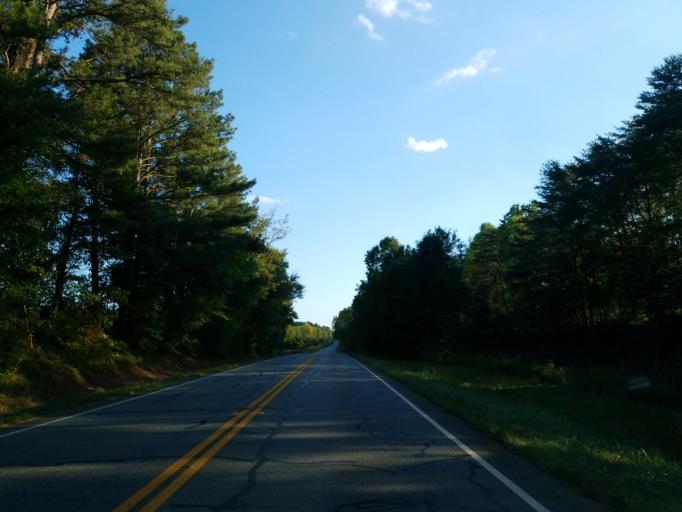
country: US
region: Georgia
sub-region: Murray County
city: Chatsworth
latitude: 34.5584
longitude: -84.7078
